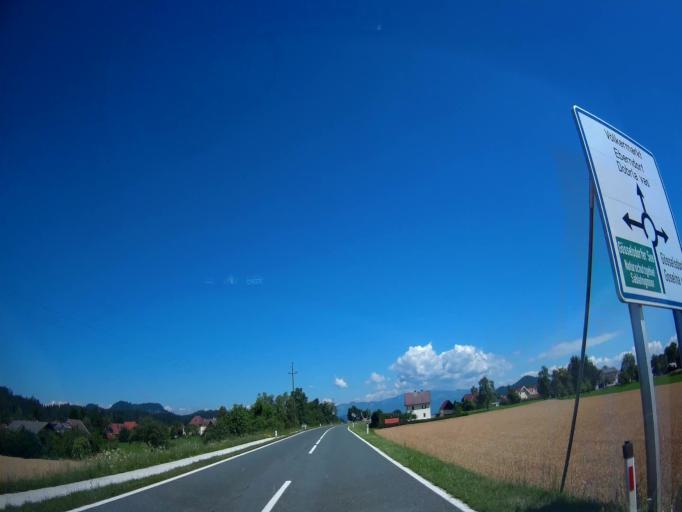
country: AT
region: Carinthia
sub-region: Politischer Bezirk Volkermarkt
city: Eberndorf
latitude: 46.5728
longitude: 14.6305
